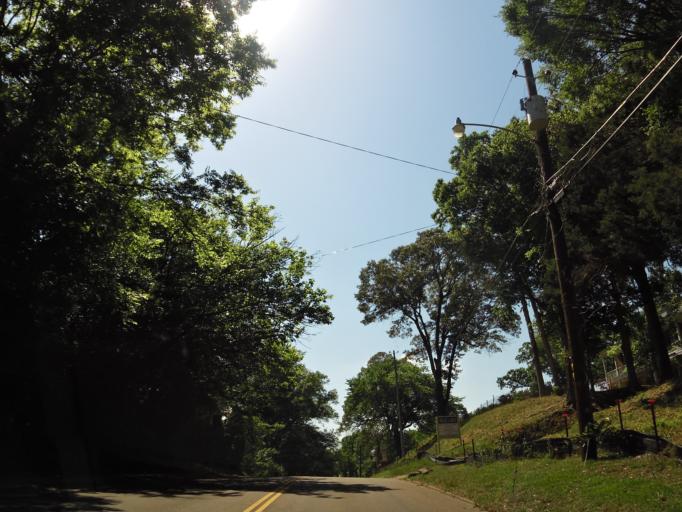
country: US
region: Mississippi
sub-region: Lafayette County
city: Oxford
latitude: 34.3658
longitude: -89.5122
